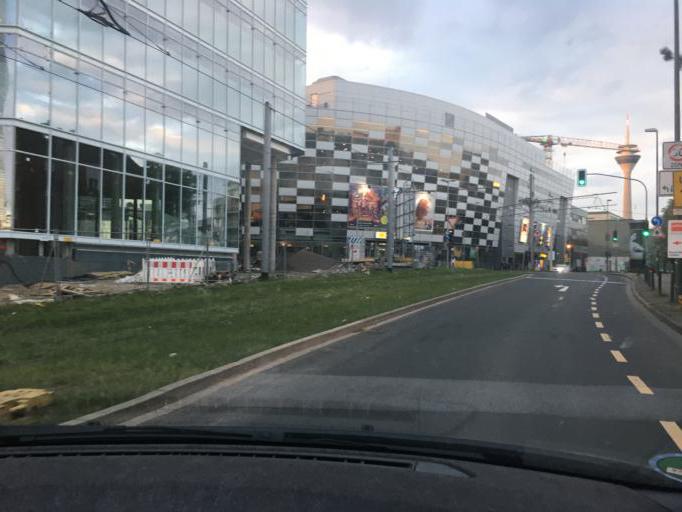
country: DE
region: North Rhine-Westphalia
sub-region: Regierungsbezirk Dusseldorf
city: Dusseldorf
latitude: 51.2125
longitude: 6.7511
